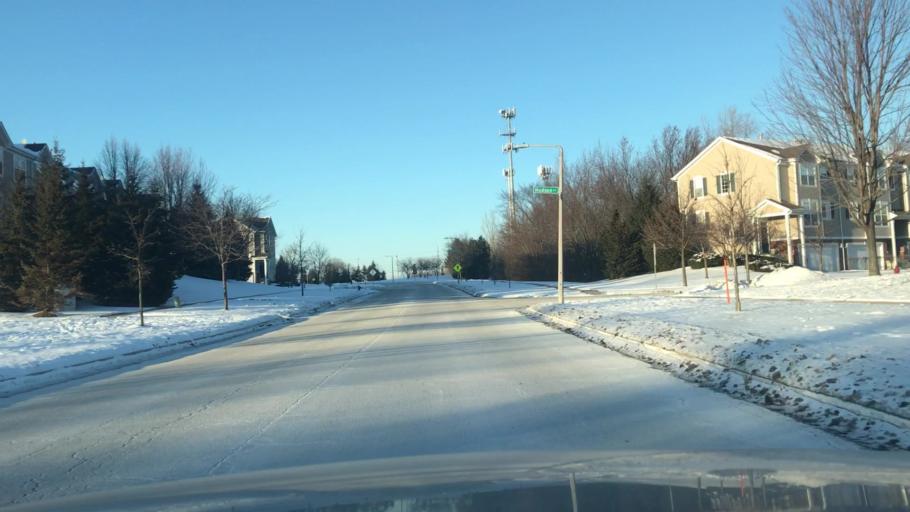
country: US
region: Illinois
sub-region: Kane County
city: Aurora
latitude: 41.7615
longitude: -88.2601
